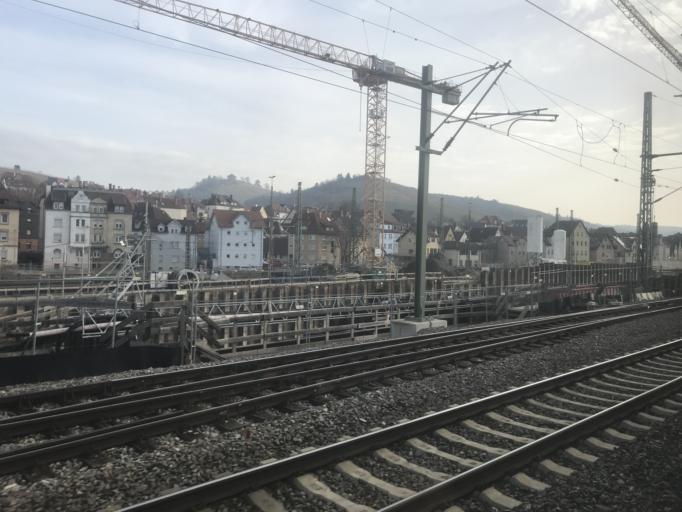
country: DE
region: Baden-Wuerttemberg
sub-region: Regierungsbezirk Stuttgart
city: Stuttgart-Ost
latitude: 48.7837
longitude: 9.2478
